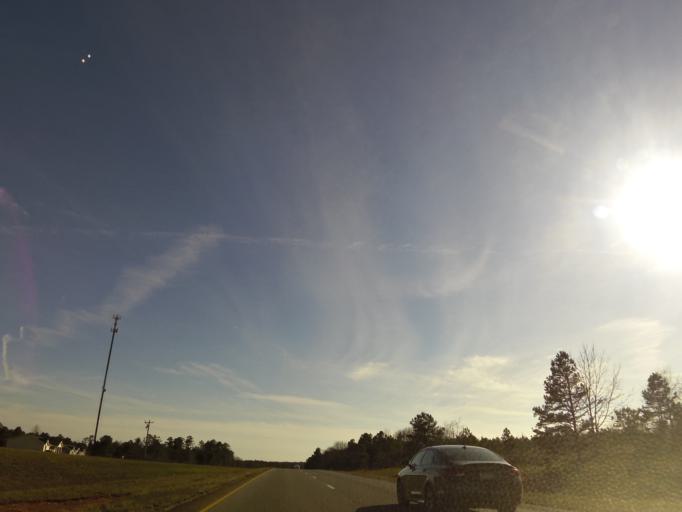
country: US
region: Georgia
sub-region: Stewart County
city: Richland
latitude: 32.1903
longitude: -84.6992
